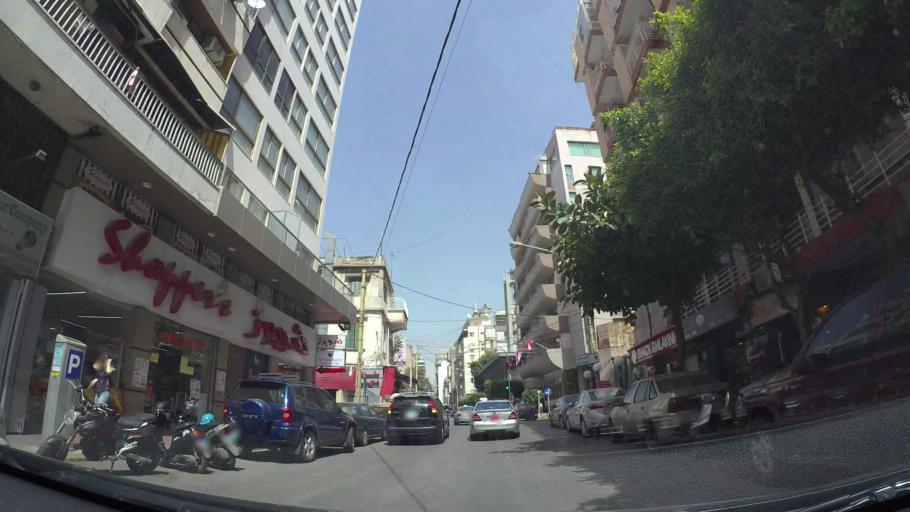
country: LB
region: Beyrouth
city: Ra's Bayrut
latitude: 33.8938
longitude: 35.4824
